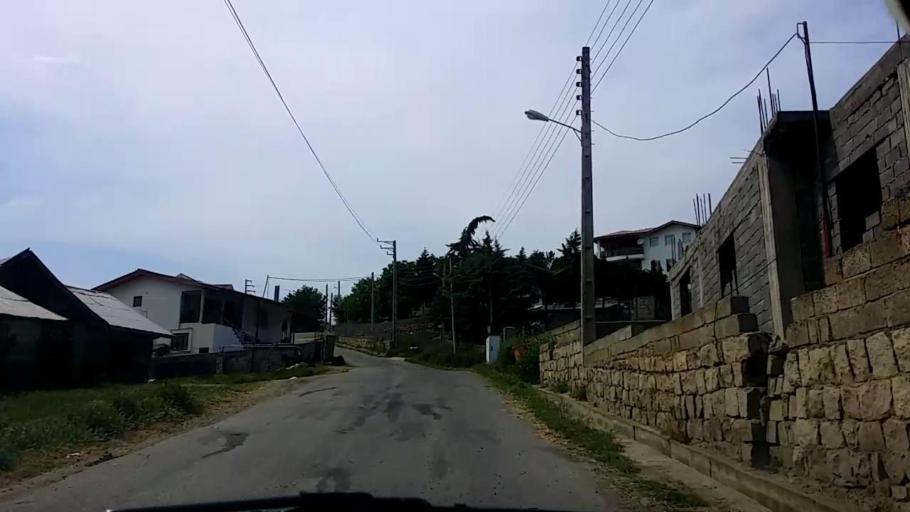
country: IR
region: Mazandaran
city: `Abbasabad
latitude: 36.5511
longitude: 51.1834
